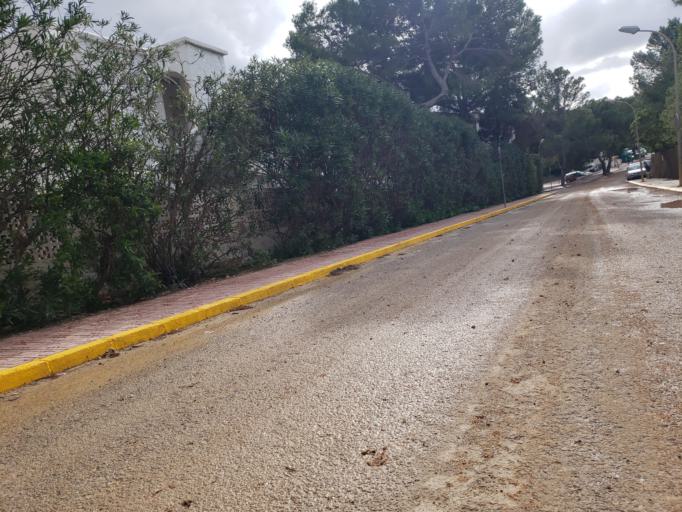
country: ES
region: Balearic Islands
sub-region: Illes Balears
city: Sant Joan de Labritja
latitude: 39.1096
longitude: 1.5098
